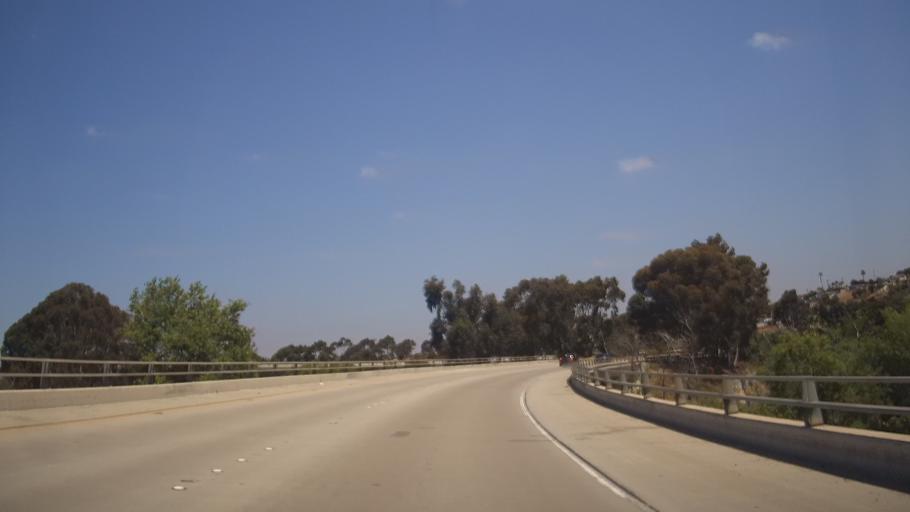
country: US
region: California
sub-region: San Diego County
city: Chula Vista
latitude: 32.6565
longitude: -117.0717
